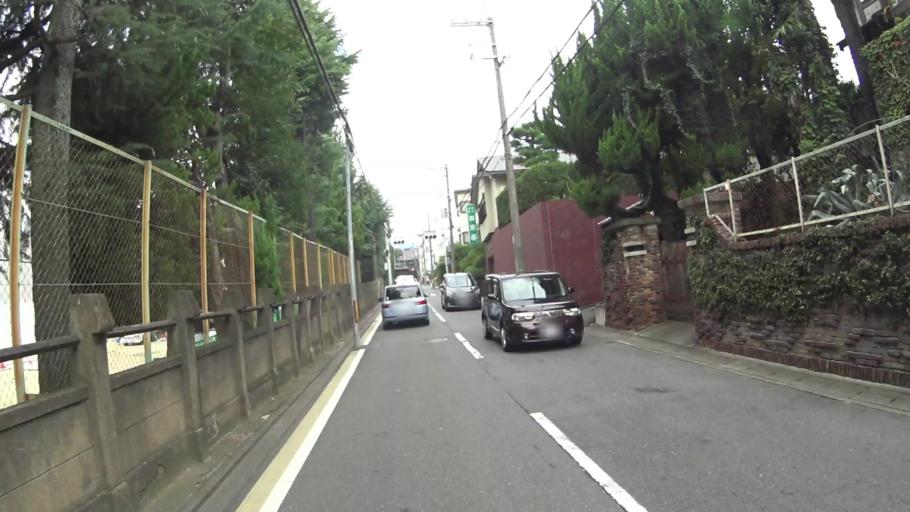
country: JP
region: Kyoto
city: Muko
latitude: 35.0116
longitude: 135.7082
